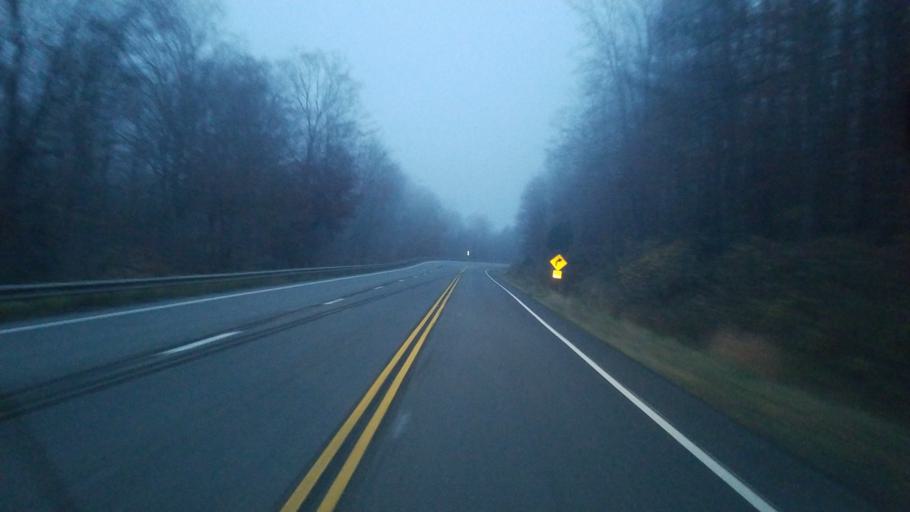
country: US
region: Pennsylvania
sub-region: McKean County
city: Smethport
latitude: 41.7234
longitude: -78.6176
